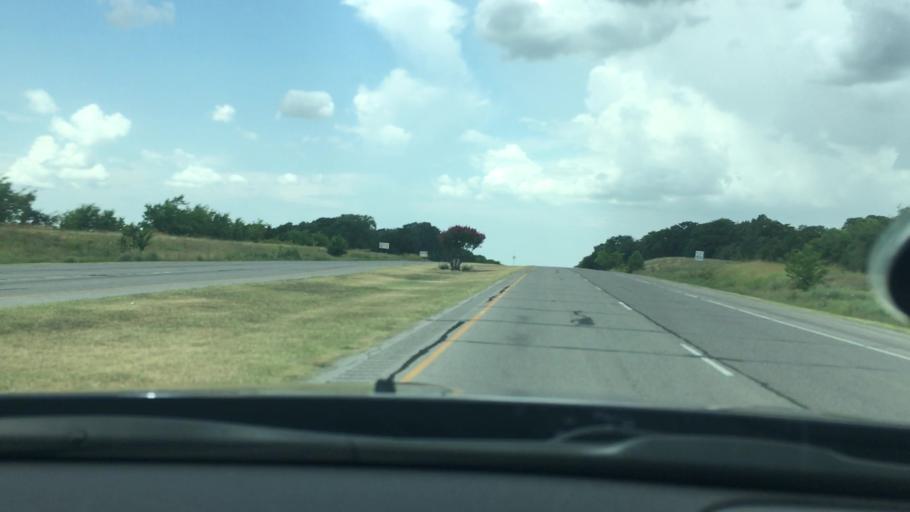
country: US
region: Oklahoma
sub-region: Carter County
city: Ardmore
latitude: 34.1394
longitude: -97.1437
